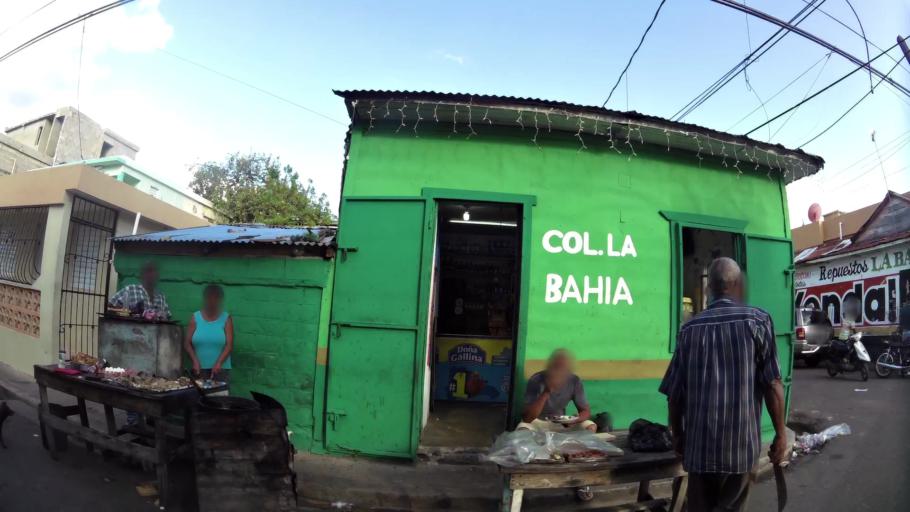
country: DO
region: Santiago
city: Santiago de los Caballeros
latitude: 19.4608
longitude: -70.7070
